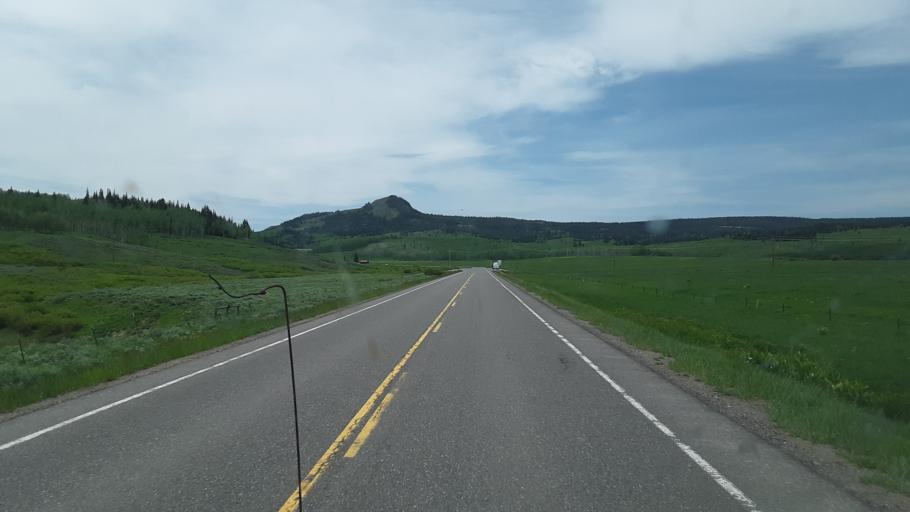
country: US
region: Colorado
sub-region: Routt County
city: Steamboat Springs
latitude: 40.3947
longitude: -106.5609
